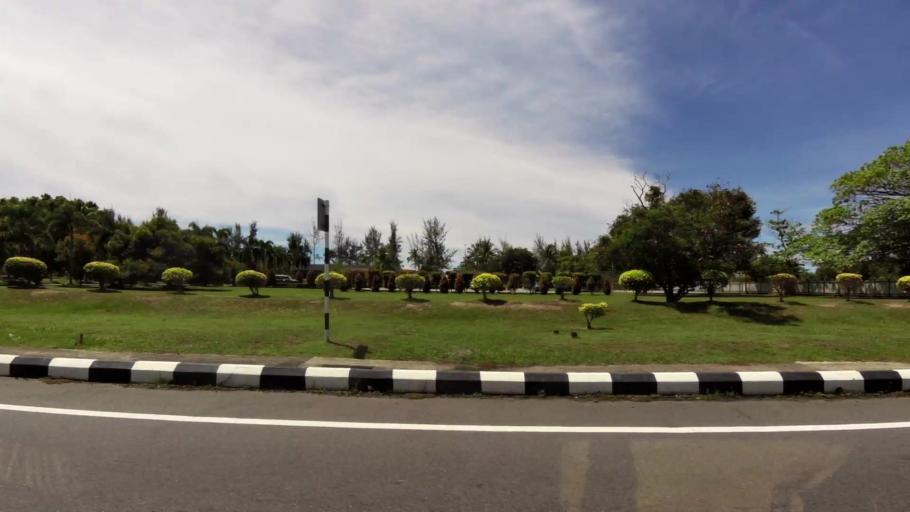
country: BN
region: Belait
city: Kuala Belait
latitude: 4.5955
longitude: 114.2479
